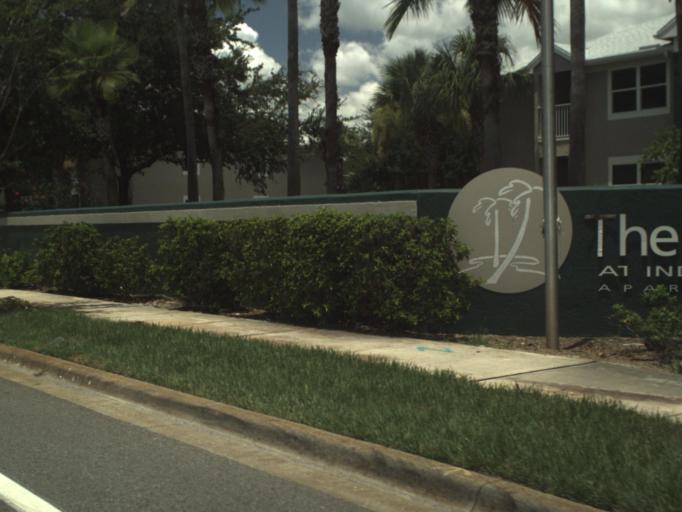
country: US
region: Florida
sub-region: Martin County
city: Palm City
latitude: 27.1602
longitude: -80.2421
